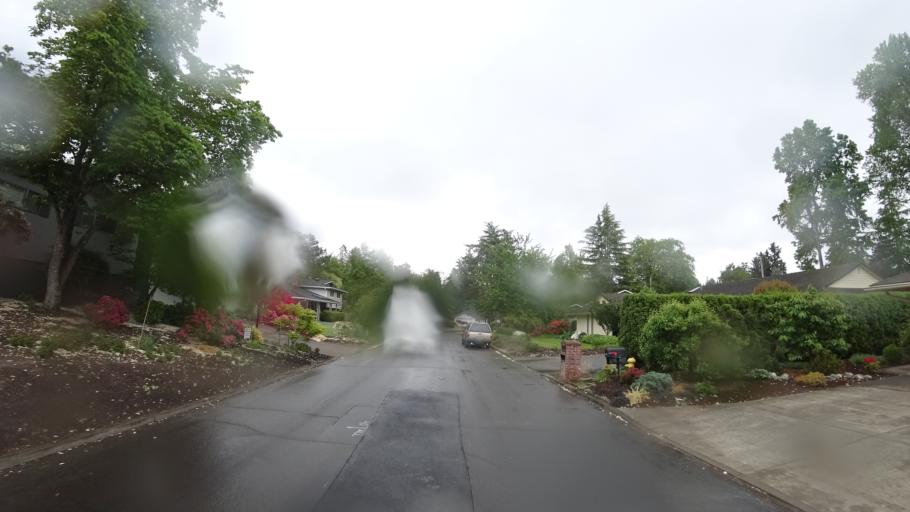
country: US
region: Oregon
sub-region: Washington County
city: Garden Home-Whitford
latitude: 45.4693
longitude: -122.7684
